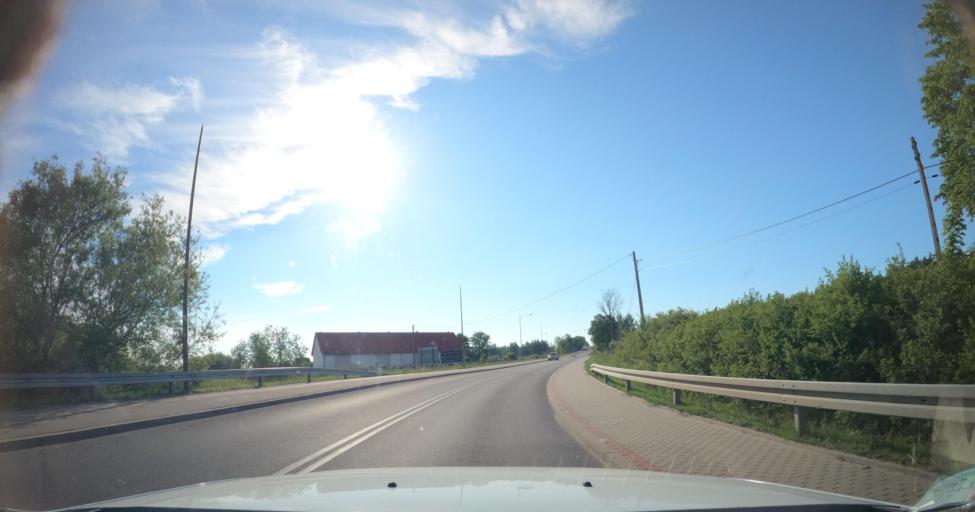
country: PL
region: Warmian-Masurian Voivodeship
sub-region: Powiat elblaski
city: Paslek
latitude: 54.0733
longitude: 19.6406
